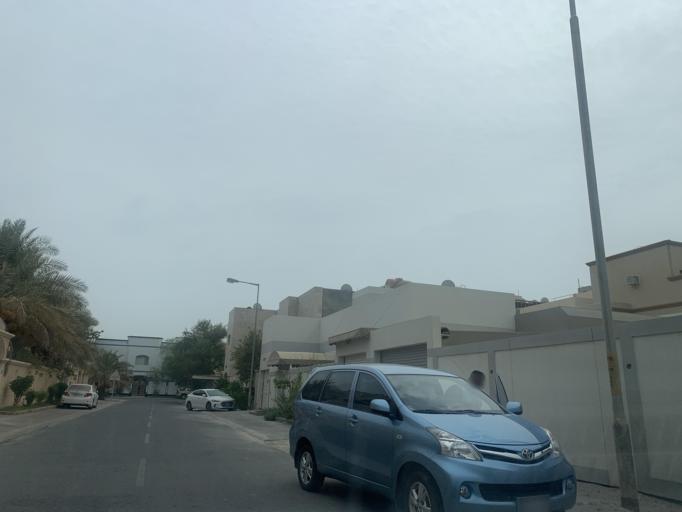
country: BH
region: Muharraq
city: Al Muharraq
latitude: 26.2787
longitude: 50.6396
